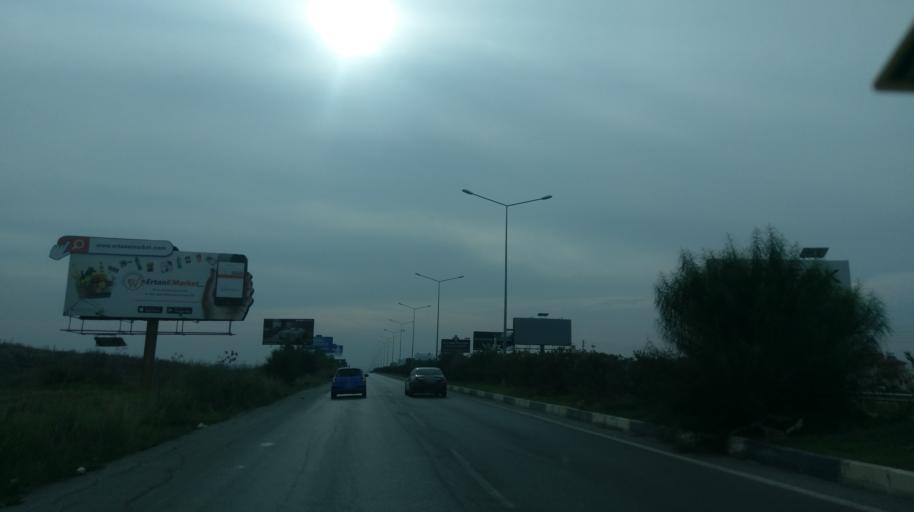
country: CY
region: Keryneia
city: Kyrenia
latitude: 35.2744
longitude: 33.2874
